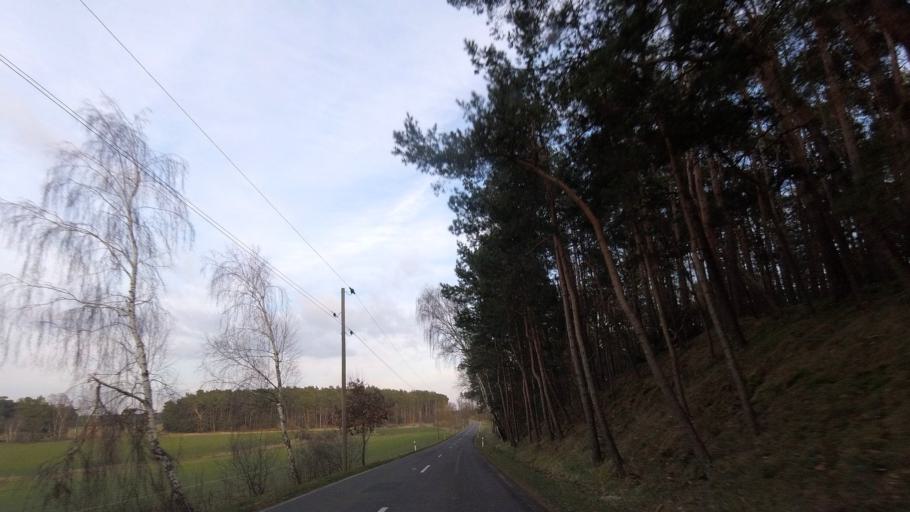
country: DE
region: Brandenburg
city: Belzig
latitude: 52.0950
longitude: 12.5963
